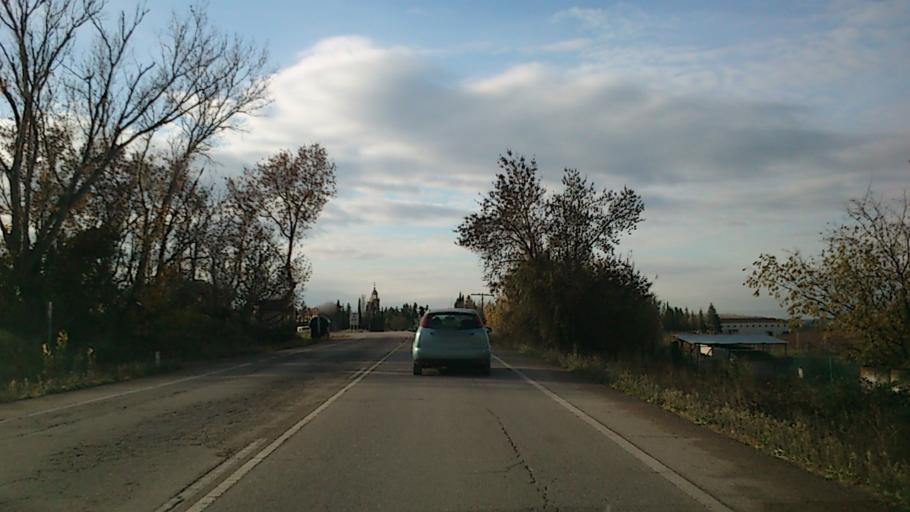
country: ES
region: Aragon
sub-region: Provincia de Zaragoza
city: Villanueva de Gallego
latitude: 41.7292
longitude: -0.8093
